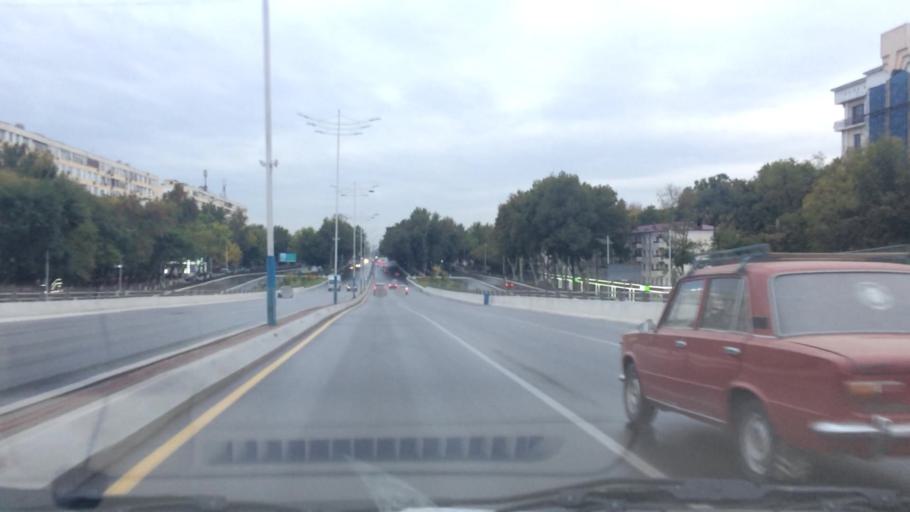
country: UZ
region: Toshkent Shahri
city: Tashkent
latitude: 41.2912
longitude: 69.2224
